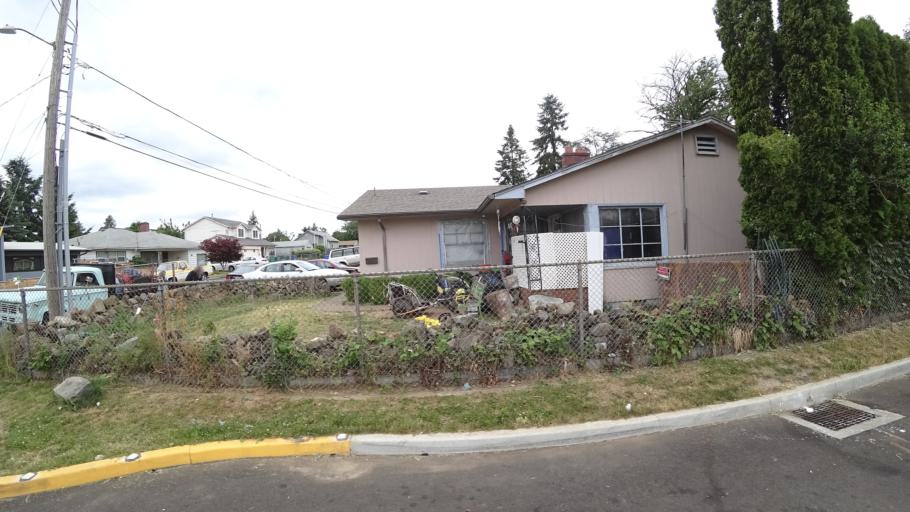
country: US
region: Oregon
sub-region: Multnomah County
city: Lents
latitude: 45.4849
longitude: -122.5748
